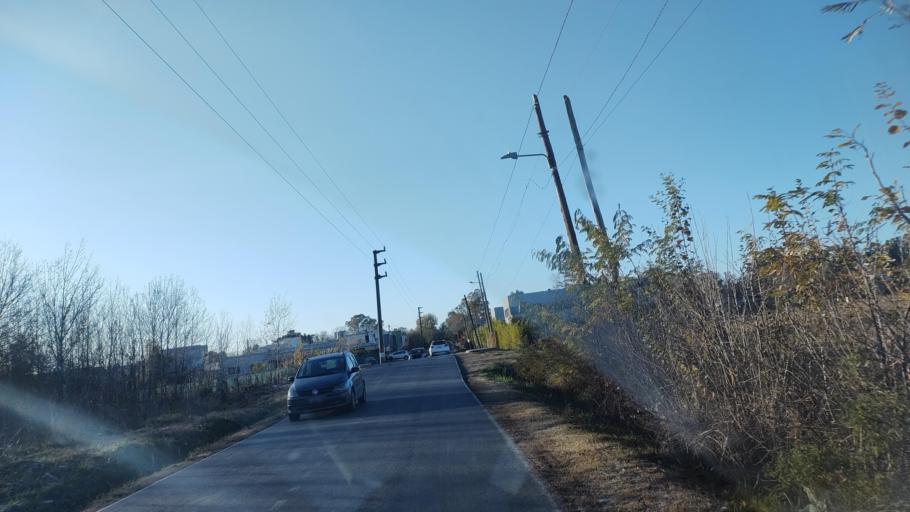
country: AR
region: Buenos Aires
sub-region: Partido de La Plata
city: La Plata
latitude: -34.8844
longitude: -58.0718
